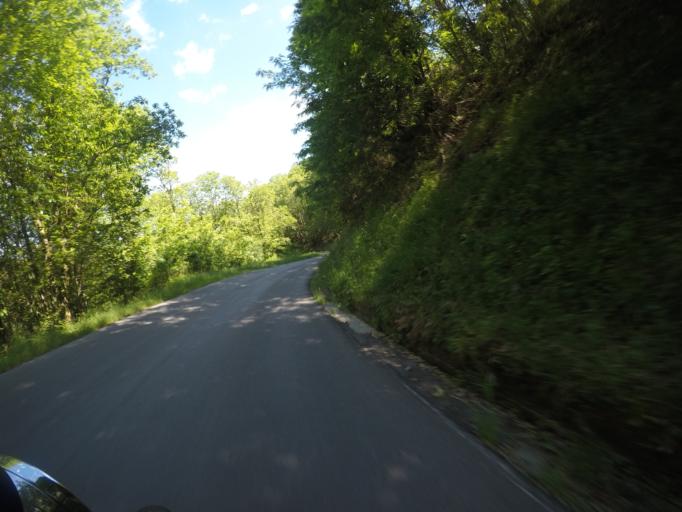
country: IT
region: Tuscany
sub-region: Provincia di Lucca
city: Careggine
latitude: 44.1315
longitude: 10.3358
